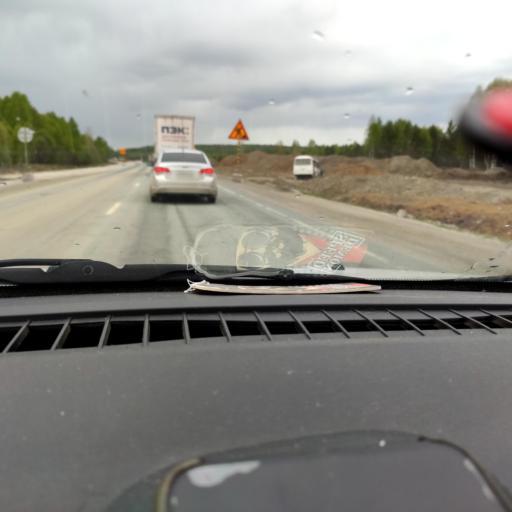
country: RU
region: Sverdlovsk
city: Bisert'
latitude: 56.8349
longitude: 58.9218
